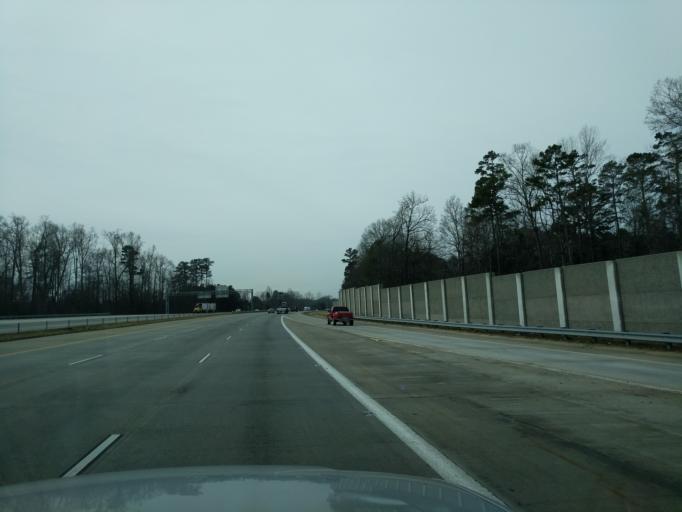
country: US
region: North Carolina
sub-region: Mecklenburg County
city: Huntersville
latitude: 35.3490
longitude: -80.8675
